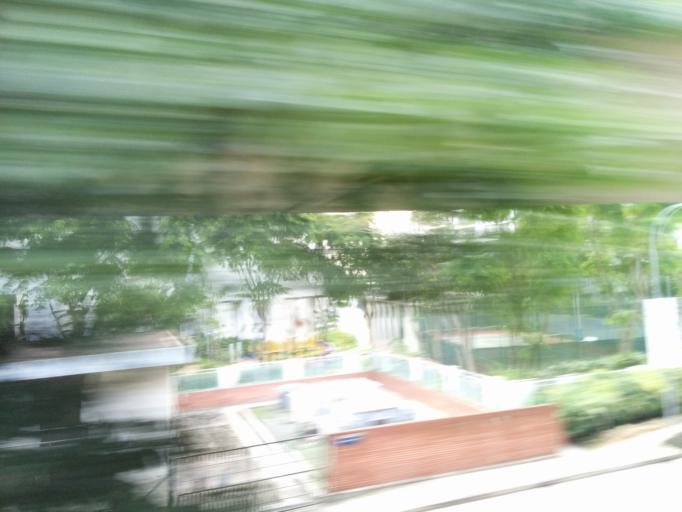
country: SG
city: Singapore
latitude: 1.2684
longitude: 103.8154
